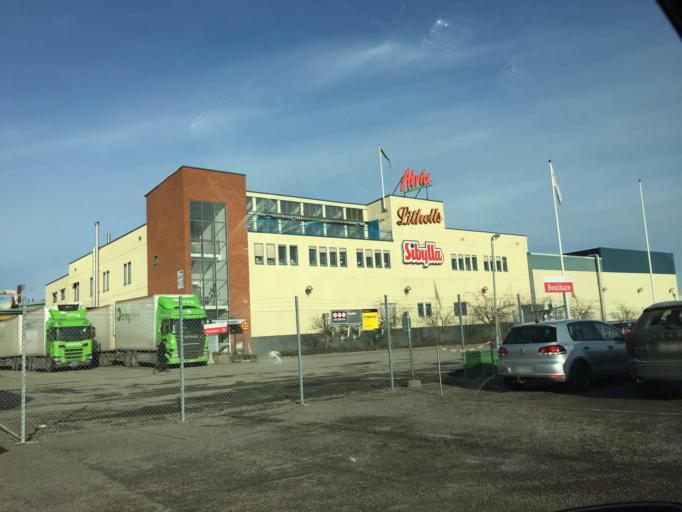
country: SE
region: OErebro
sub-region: Hallsbergs Kommun
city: Skollersta
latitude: 59.1371
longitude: 15.3556
